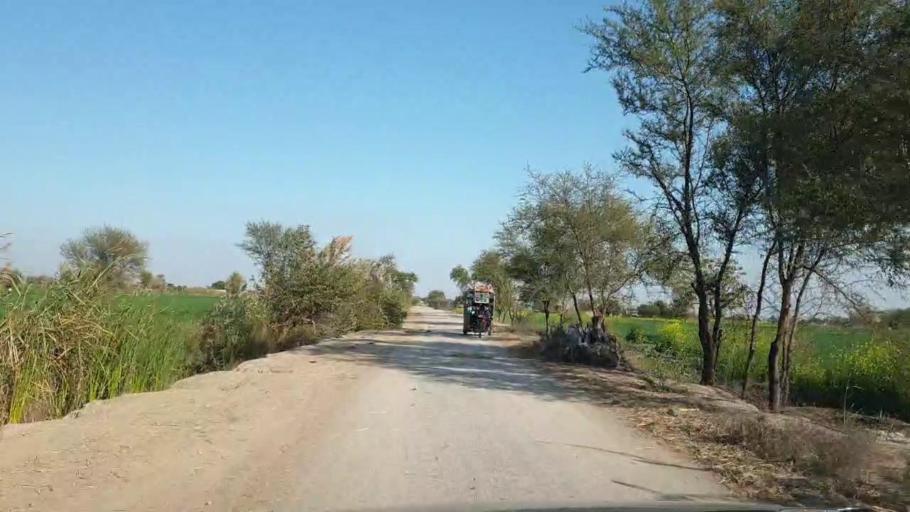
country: PK
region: Sindh
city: Khadro
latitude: 26.1898
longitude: 68.7562
